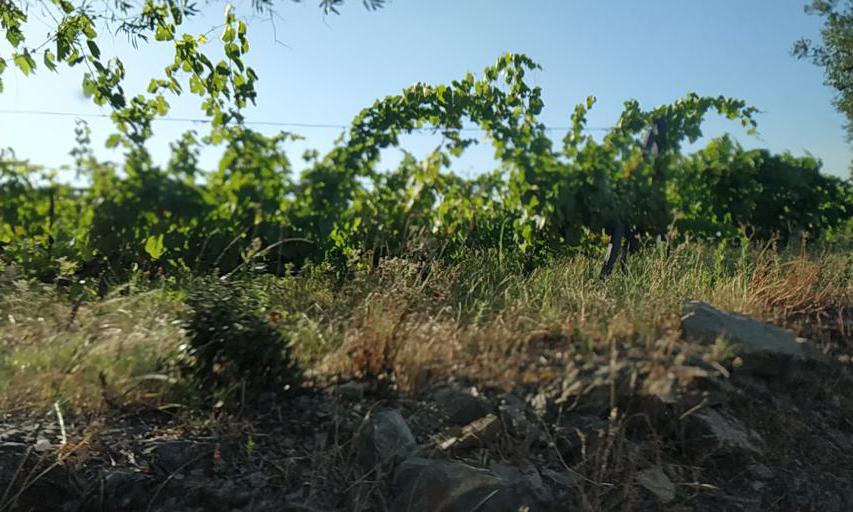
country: PT
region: Viseu
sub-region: Sao Joao da Pesqueira
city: Sao Joao da Pesqueira
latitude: 41.1560
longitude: -7.4199
